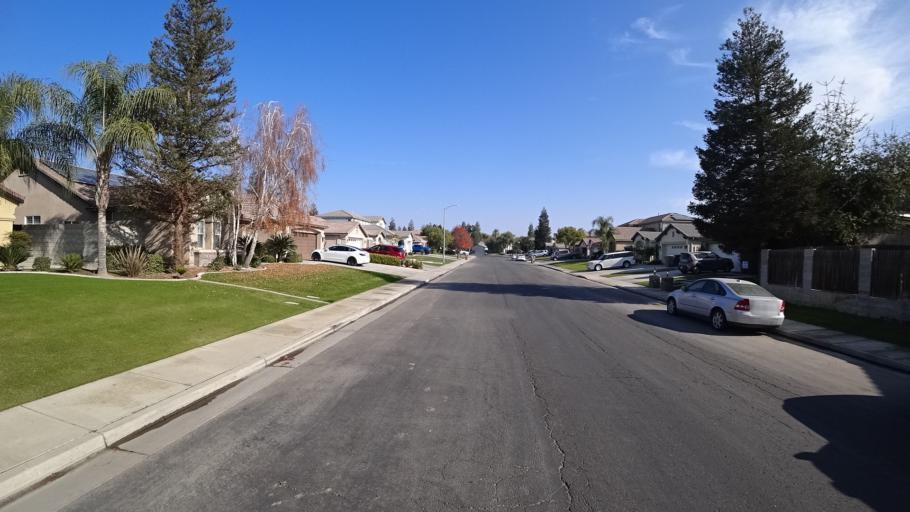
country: US
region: California
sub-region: Kern County
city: Rosedale
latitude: 35.3603
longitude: -119.1668
